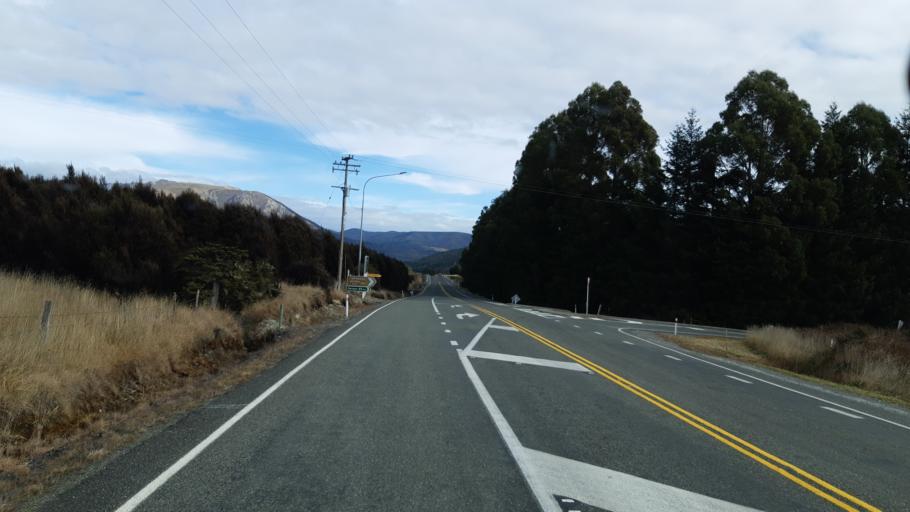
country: NZ
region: Tasman
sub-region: Tasman District
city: Wakefield
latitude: -41.7848
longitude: 172.8957
